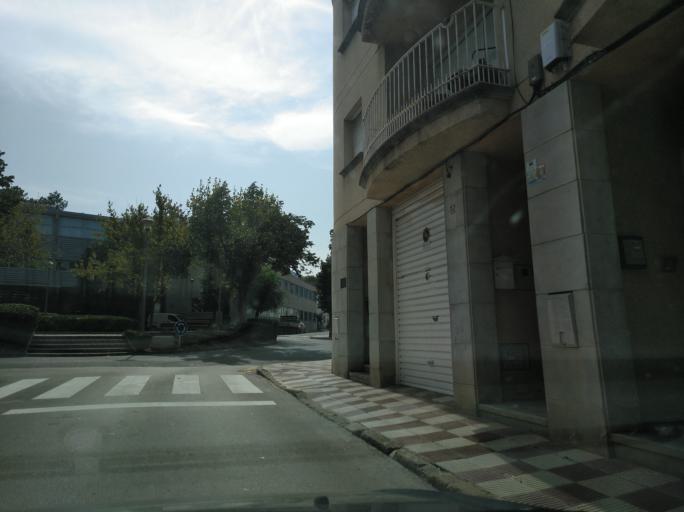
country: ES
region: Catalonia
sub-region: Provincia de Girona
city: Angles
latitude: 41.9566
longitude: 2.6335
